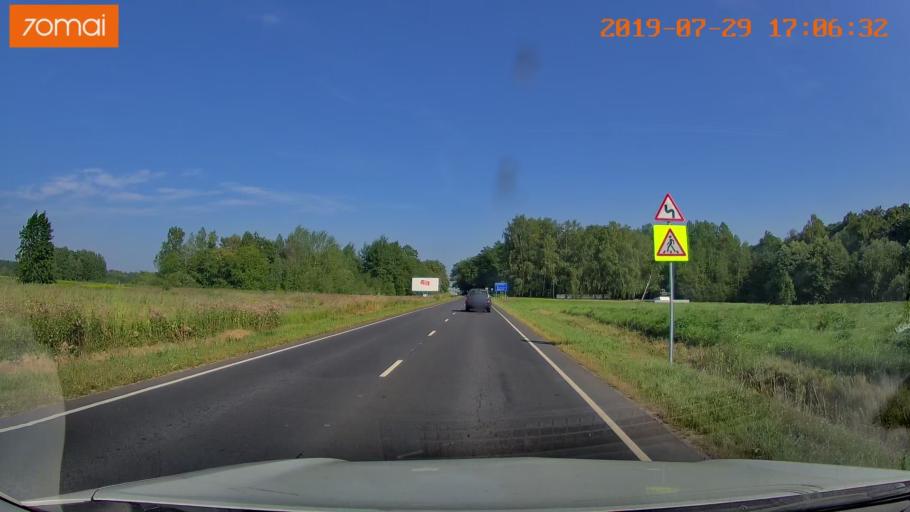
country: RU
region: Kaliningrad
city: Vzmorye
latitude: 54.8198
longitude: 20.3093
